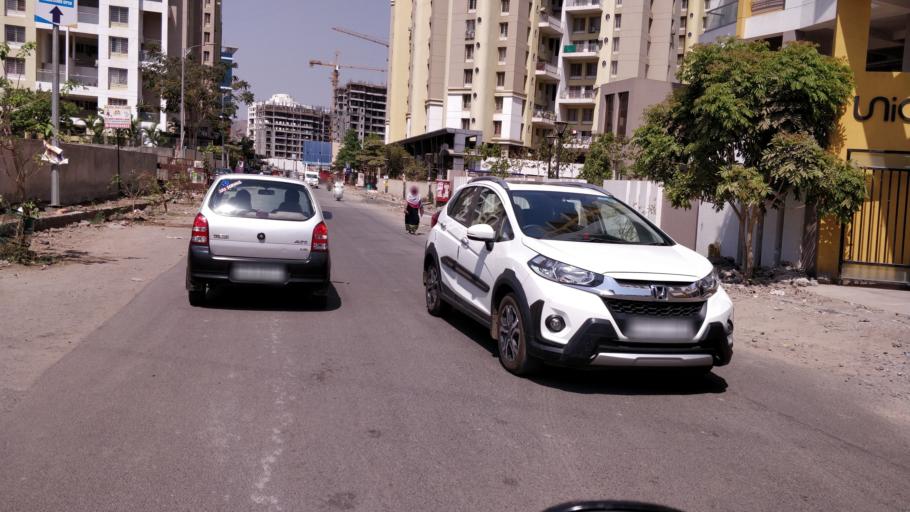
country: IN
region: Maharashtra
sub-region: Pune Division
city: Kharakvasla
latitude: 18.5112
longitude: 73.7766
